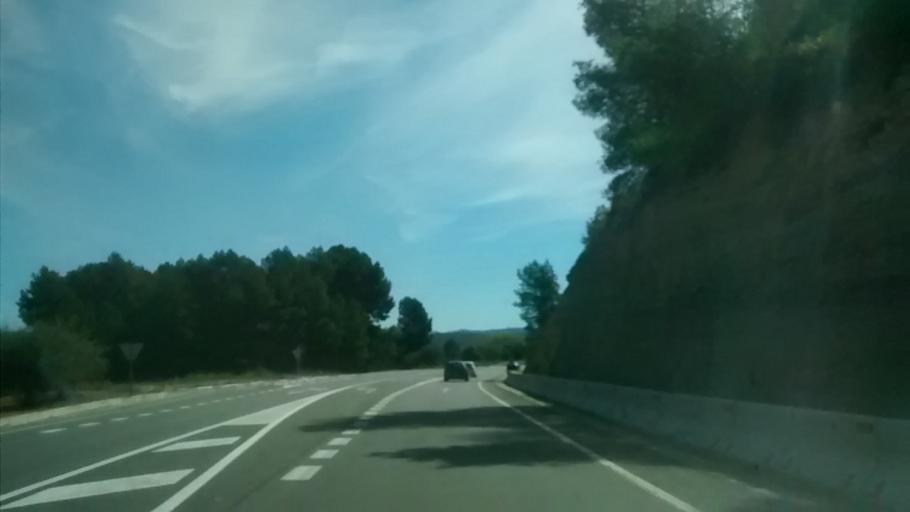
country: ES
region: Catalonia
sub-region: Provincia de Tarragona
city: Flix
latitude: 41.2230
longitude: 0.5446
